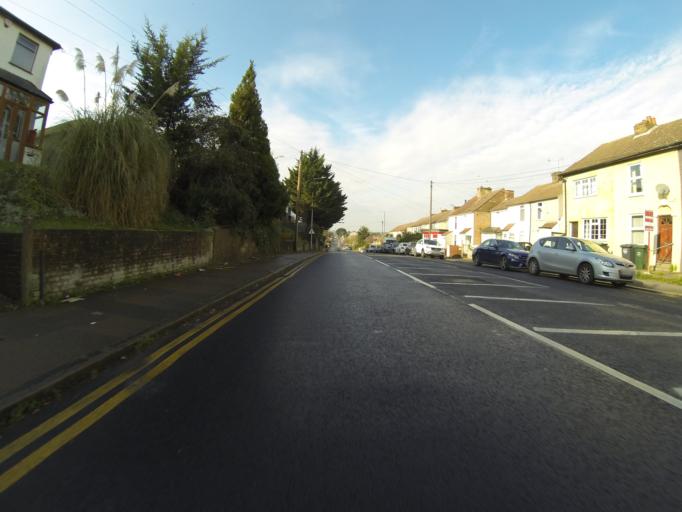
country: GB
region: England
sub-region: Kent
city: Dartford
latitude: 51.4477
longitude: 0.1971
